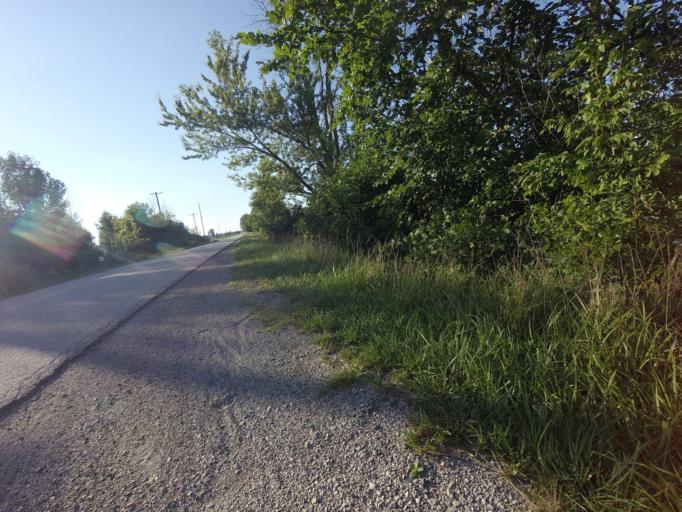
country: CA
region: Ontario
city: Goderich
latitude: 43.7540
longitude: -81.6712
